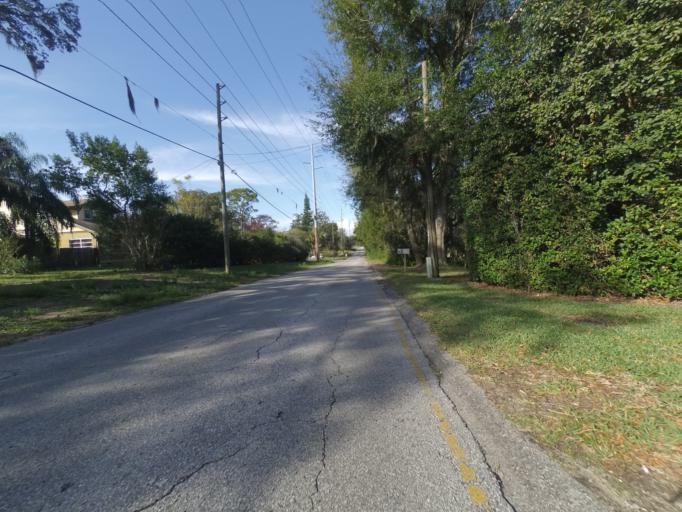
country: US
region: Florida
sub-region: Lake County
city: Eustis
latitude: 28.8310
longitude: -81.6834
